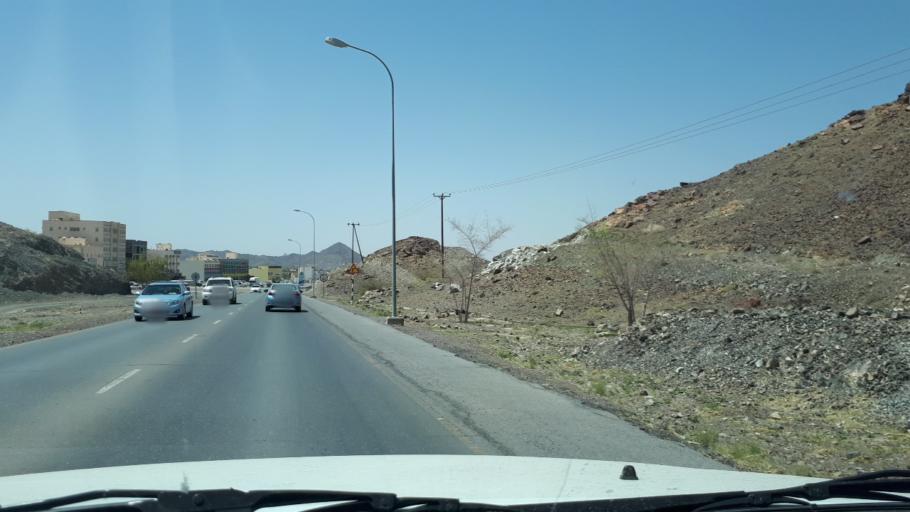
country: OM
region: Muhafazat ad Dakhiliyah
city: Bahla'
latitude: 22.9542
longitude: 57.2872
